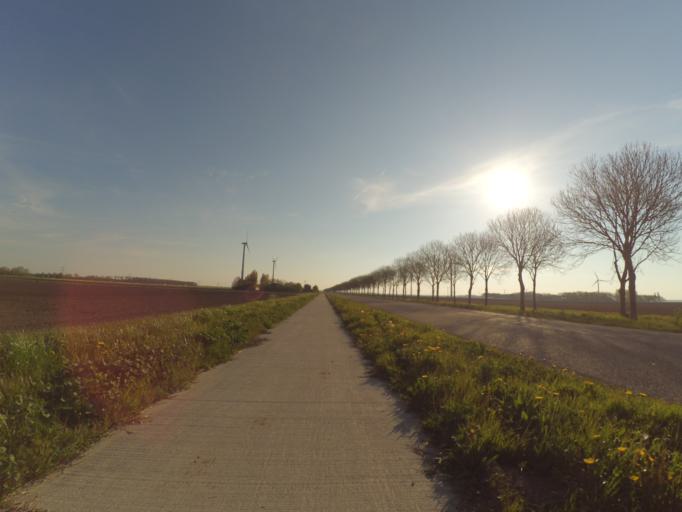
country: NL
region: Utrecht
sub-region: Gemeente Bunschoten
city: Spakenburg
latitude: 52.3998
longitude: 5.3636
